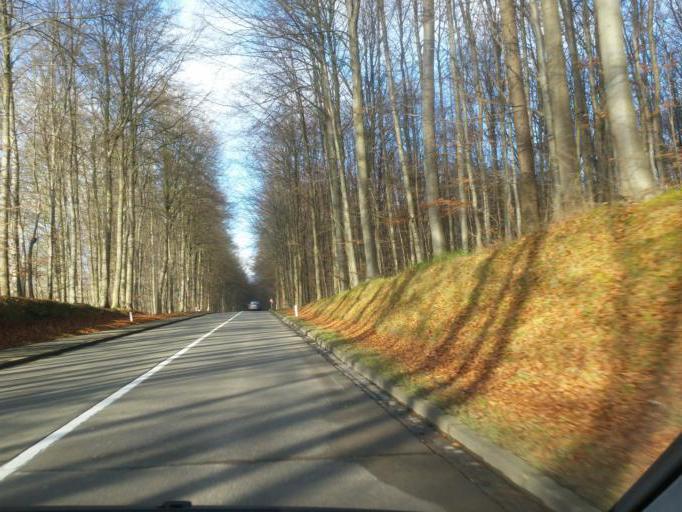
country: BE
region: Flanders
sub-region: Provincie Vlaams-Brabant
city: Hoeilaart
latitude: 50.7710
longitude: 4.4404
